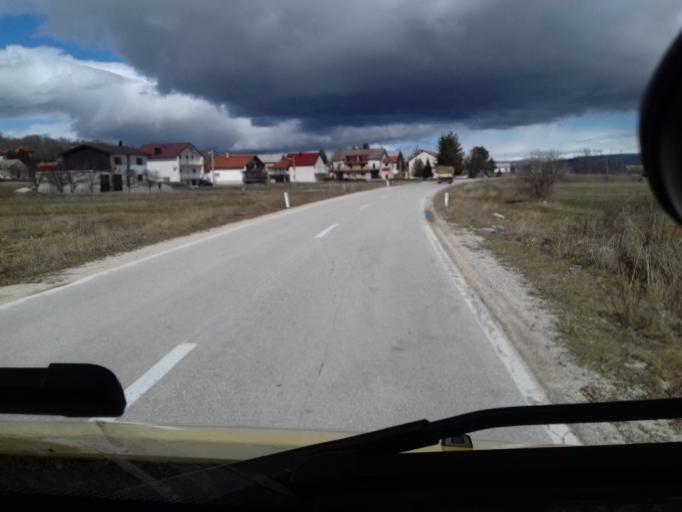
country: BA
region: Federation of Bosnia and Herzegovina
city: Dreznica
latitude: 43.5935
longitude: 17.2731
